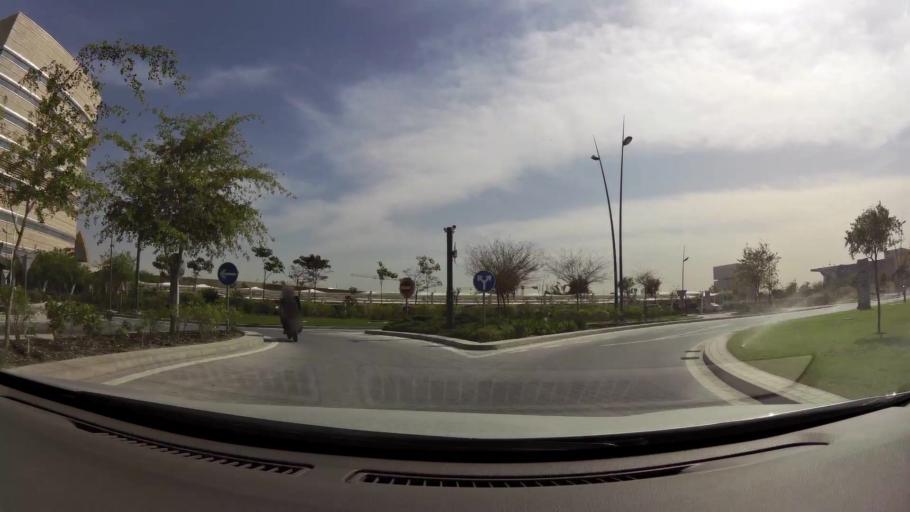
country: QA
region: Baladiyat ar Rayyan
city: Ar Rayyan
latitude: 25.3226
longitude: 51.4422
